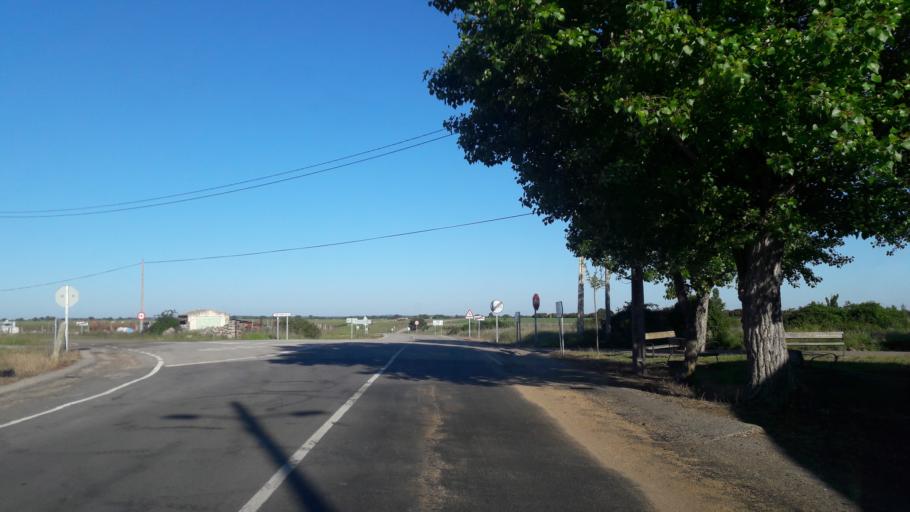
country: ES
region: Castille and Leon
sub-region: Provincia de Salamanca
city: Boada
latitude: 40.8157
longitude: -6.3086
